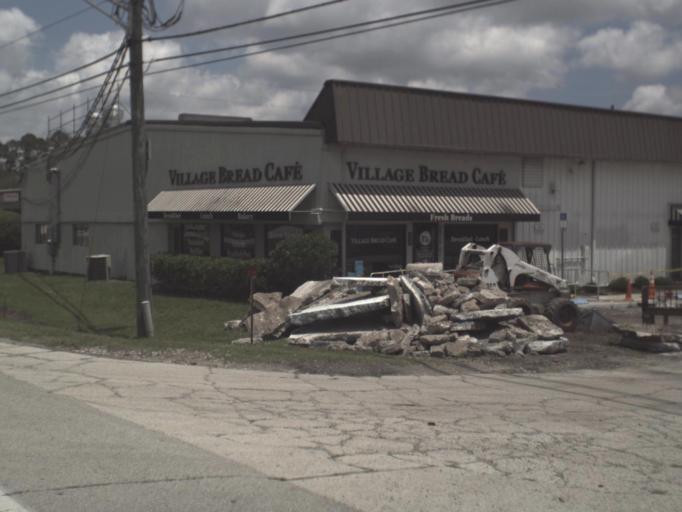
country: US
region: Florida
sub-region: Duval County
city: Jacksonville
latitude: 30.2699
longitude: -81.6209
